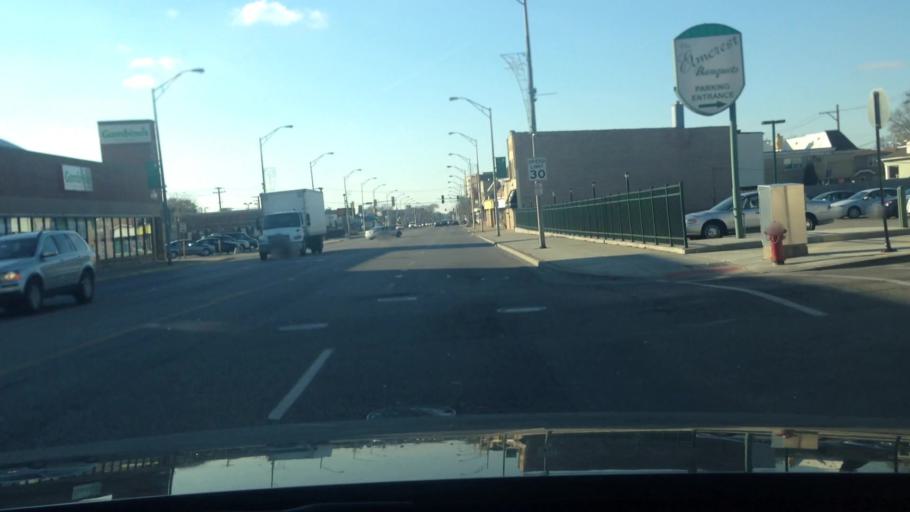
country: US
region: Illinois
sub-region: Cook County
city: Elmwood Park
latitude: 41.9248
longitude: -87.8110
